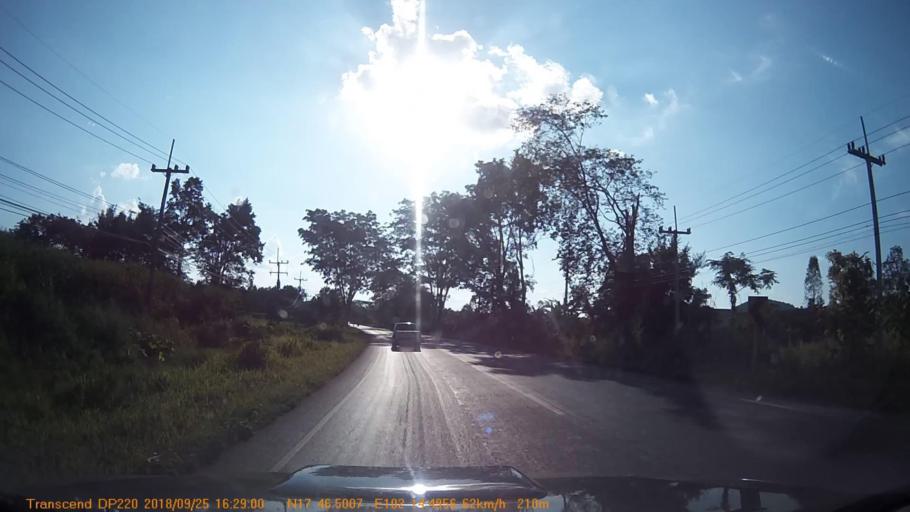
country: TH
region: Changwat Udon Thani
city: Nam Som
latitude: 17.7750
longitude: 102.2415
